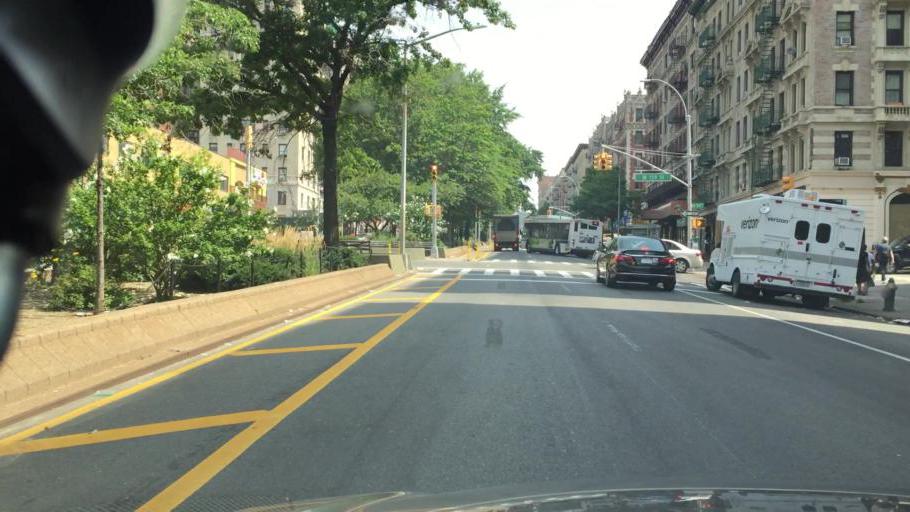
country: US
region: New Jersey
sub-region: Bergen County
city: Fort Lee
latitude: 40.8350
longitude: -73.9441
